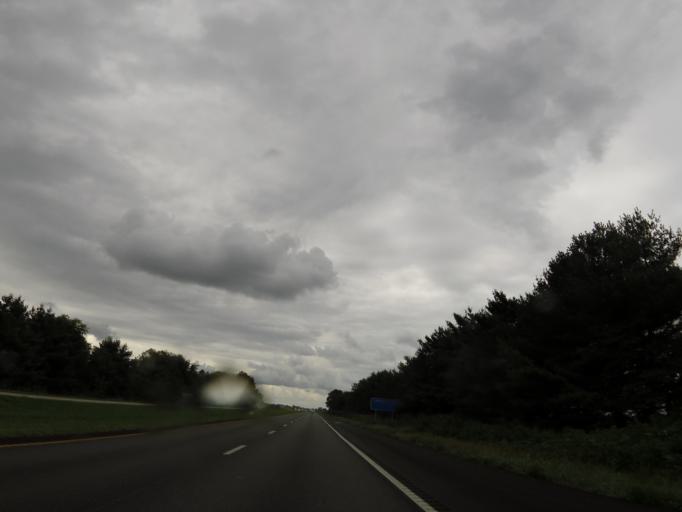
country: US
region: Missouri
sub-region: Mississippi County
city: Charleston
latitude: 36.9106
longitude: -89.3299
